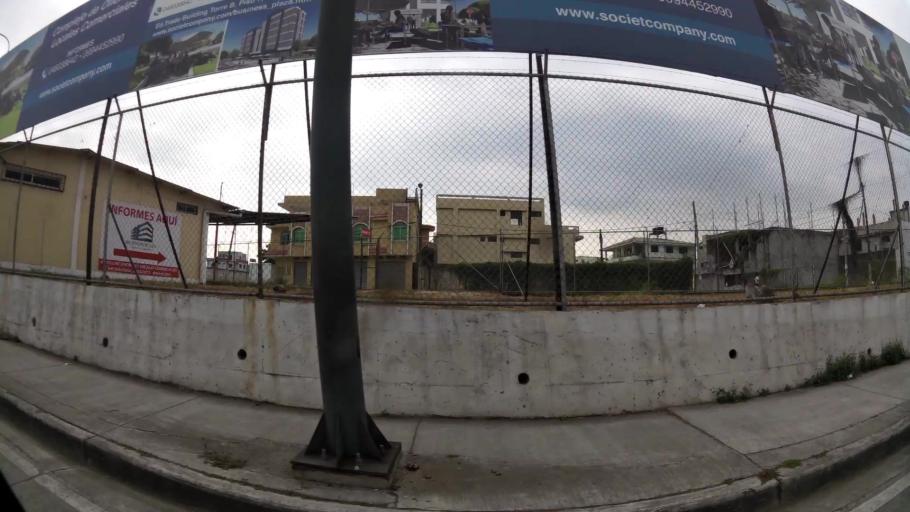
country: EC
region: Guayas
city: Eloy Alfaro
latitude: -2.1383
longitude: -79.8828
